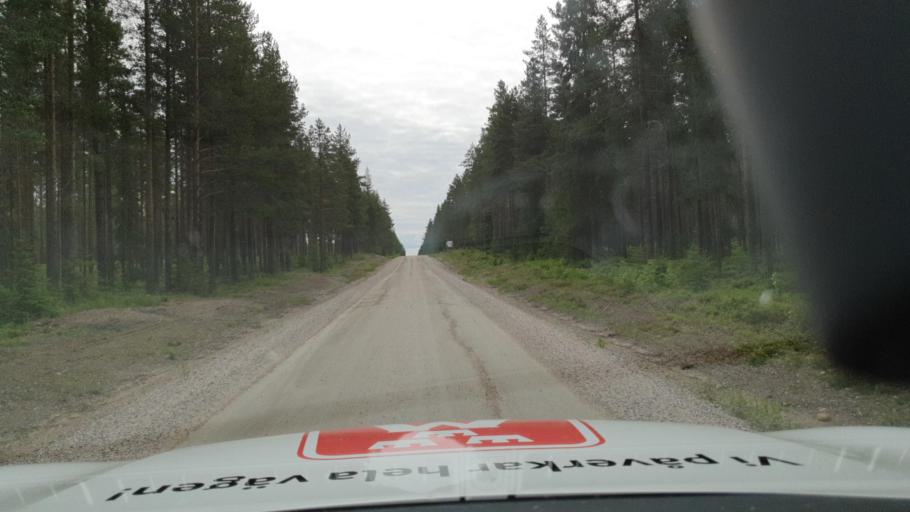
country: SE
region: Vaesterbotten
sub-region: Skelleftea Kommun
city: Forsbacka
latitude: 64.6495
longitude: 20.4478
